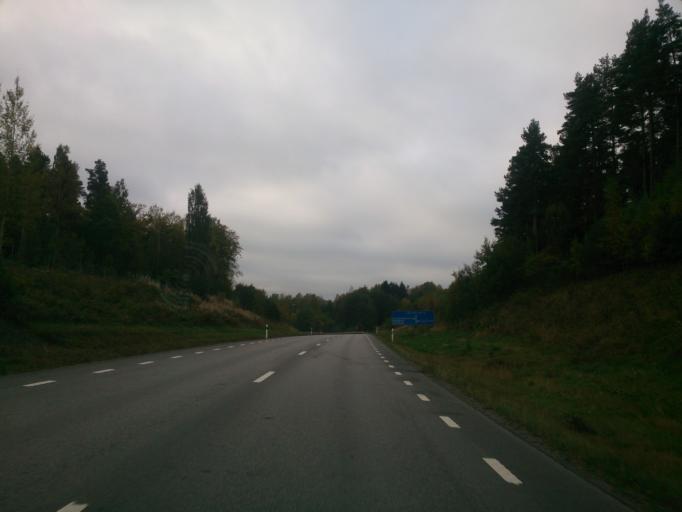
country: SE
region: OEstergoetland
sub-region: Atvidabergs Kommun
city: Atvidaberg
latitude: 58.1877
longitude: 16.0235
